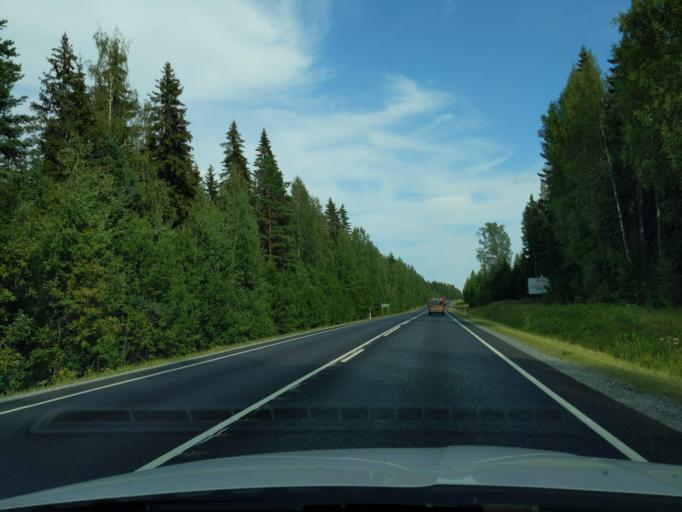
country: FI
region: Haeme
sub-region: Haemeenlinna
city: Hauho
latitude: 61.1732
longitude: 24.6016
